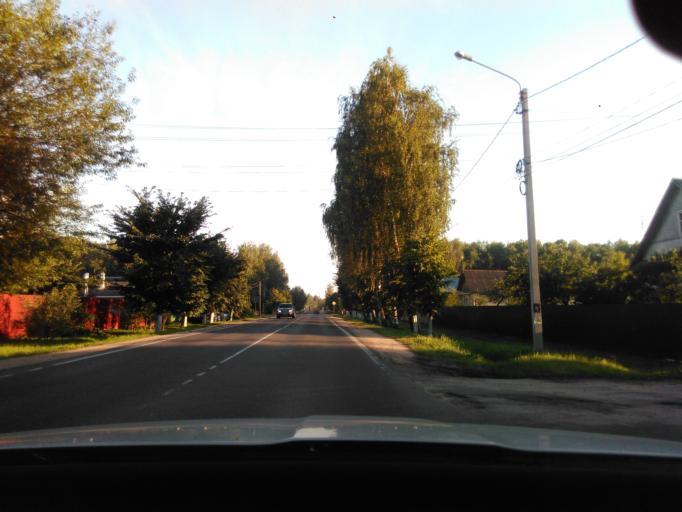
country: RU
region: Tverskaya
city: Konakovo
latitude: 56.6870
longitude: 36.7627
